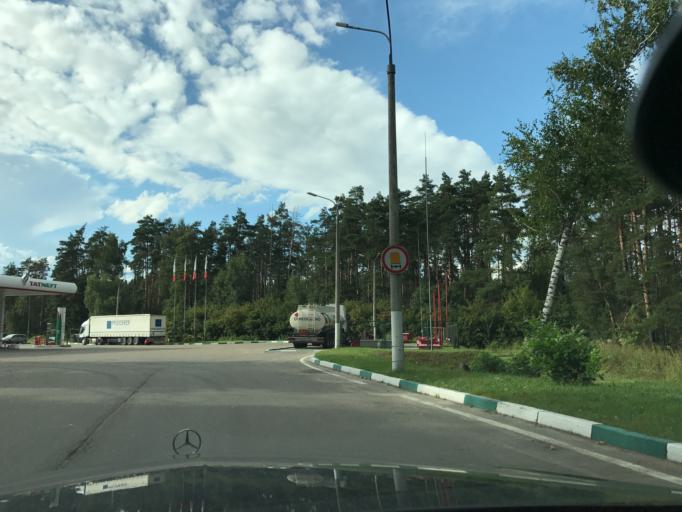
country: RU
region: Moskovskaya
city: Zarya
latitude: 55.8083
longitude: 38.0640
